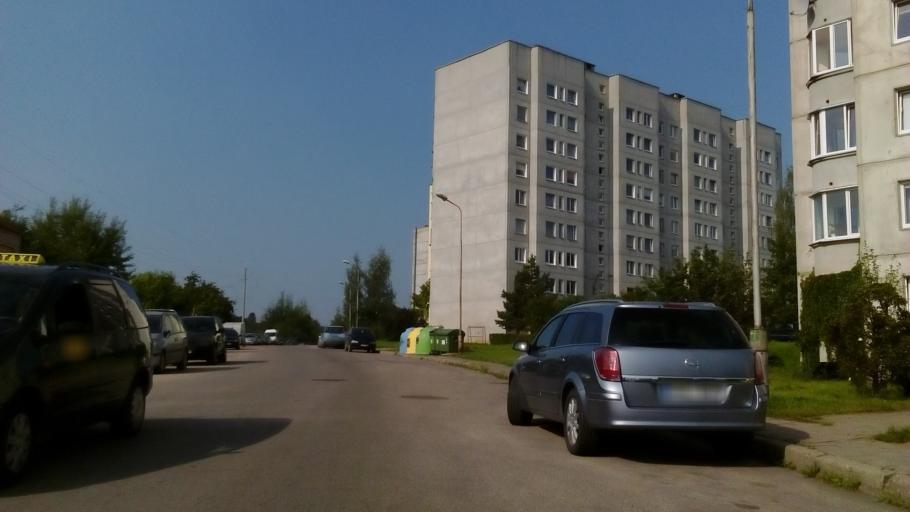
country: LT
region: Alytaus apskritis
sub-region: Alytus
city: Alytus
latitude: 54.3889
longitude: 24.0223
